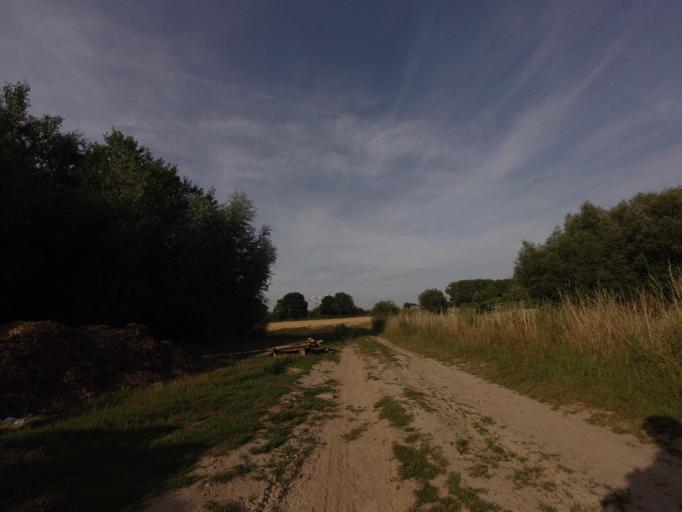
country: BE
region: Flanders
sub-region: Provincie Vlaams-Brabant
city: Grimbergen
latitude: 50.9182
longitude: 4.3759
